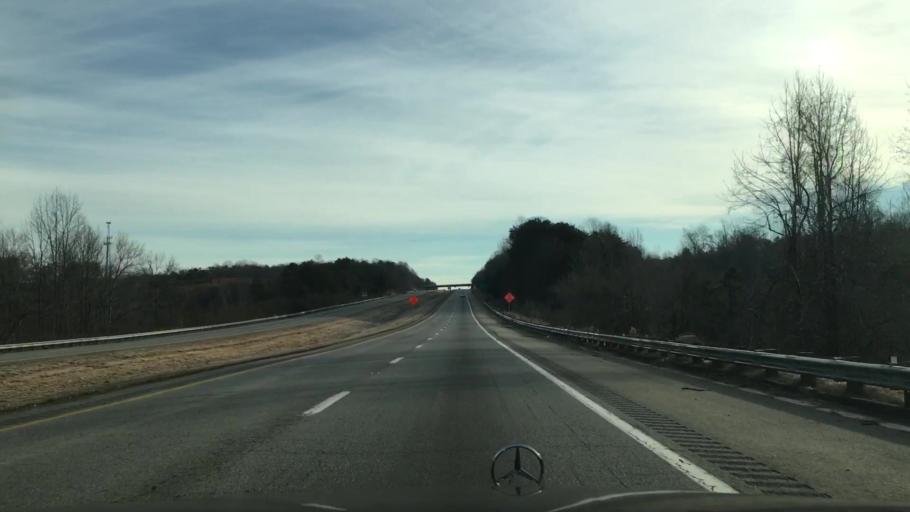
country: US
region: Virginia
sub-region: City of Danville
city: Danville
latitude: 36.5454
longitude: -79.4119
